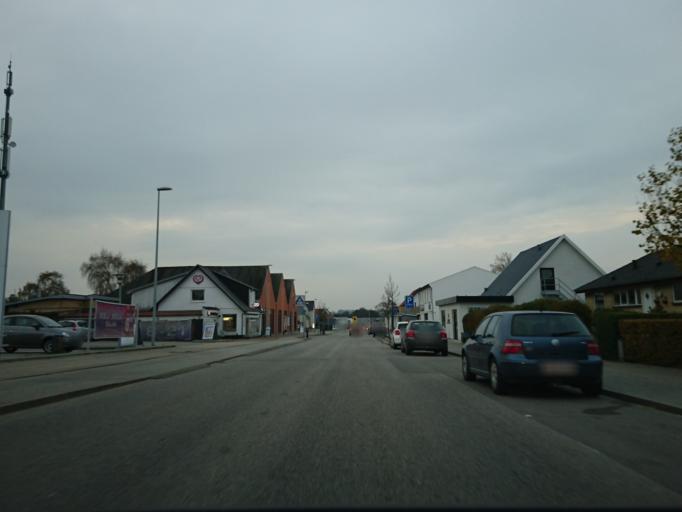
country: DK
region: North Denmark
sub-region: Alborg Kommune
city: Aalborg
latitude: 57.0091
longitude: 9.9263
